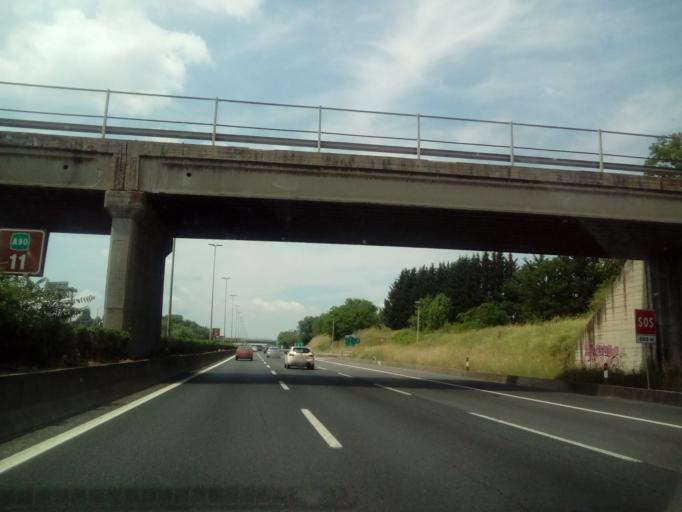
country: IT
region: Latium
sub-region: Citta metropolitana di Roma Capitale
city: Colle Verde
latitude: 41.9457
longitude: 12.5915
